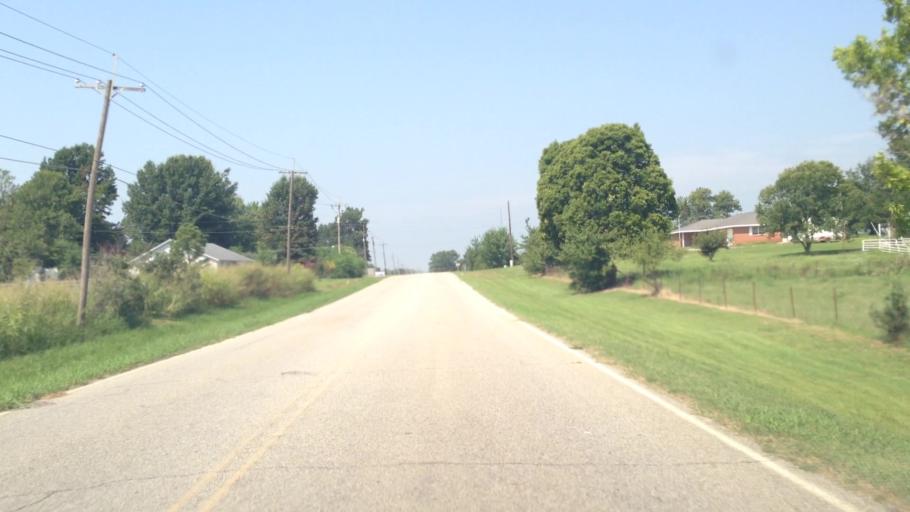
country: US
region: Oklahoma
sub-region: Craig County
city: Vinita
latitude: 36.6560
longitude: -95.1287
